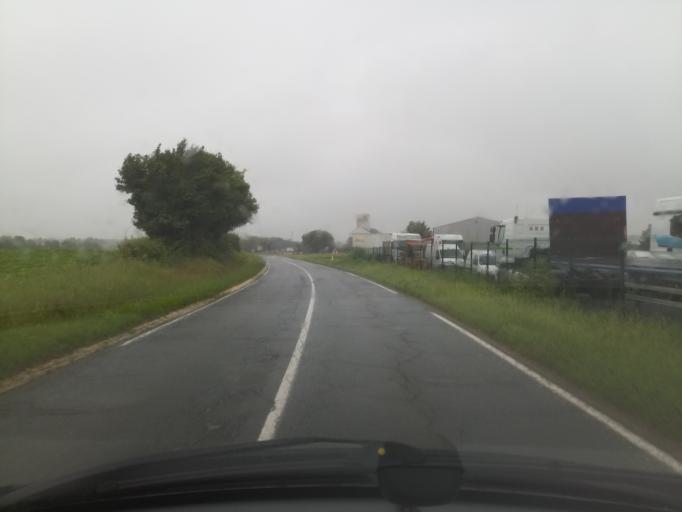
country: FR
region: Poitou-Charentes
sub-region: Departement de la Charente-Maritime
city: Saint-Jean-de-Liversay
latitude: 46.2312
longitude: -0.8805
